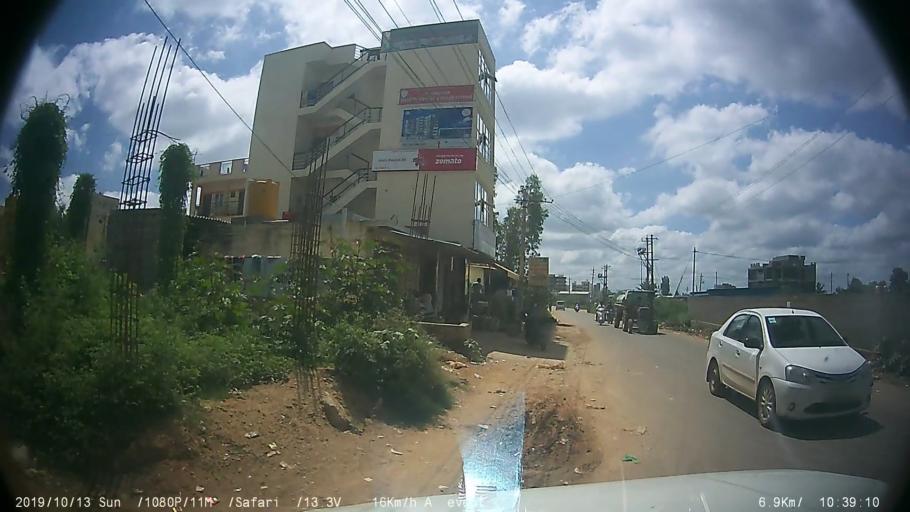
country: IN
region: Karnataka
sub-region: Bangalore Urban
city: Anekal
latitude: 12.8375
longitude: 77.6454
